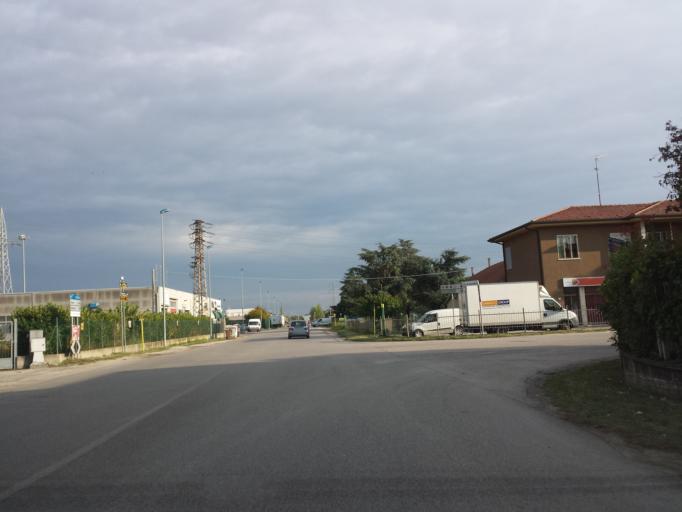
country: IT
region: Veneto
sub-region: Provincia di Rovigo
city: Rovigo
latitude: 45.0450
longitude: 11.7960
